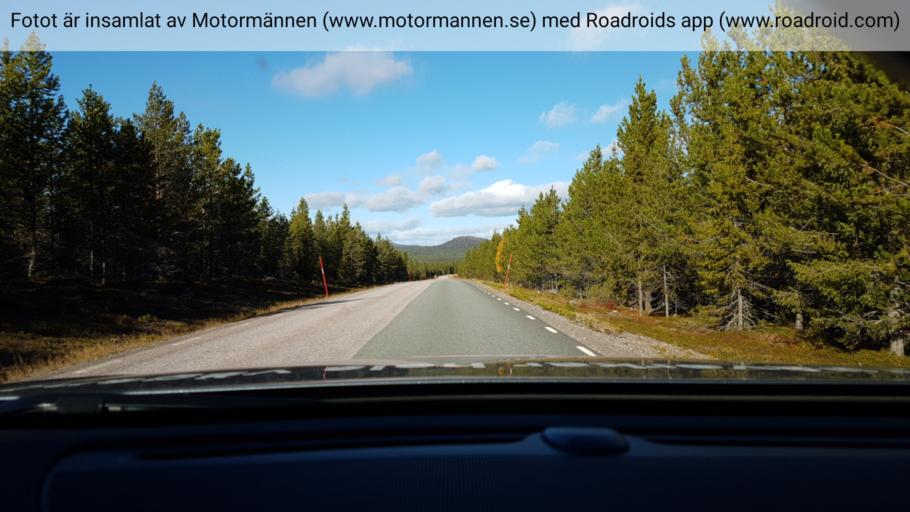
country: SE
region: Norrbotten
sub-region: Arjeplogs Kommun
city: Arjeplog
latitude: 65.8424
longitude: 18.4151
